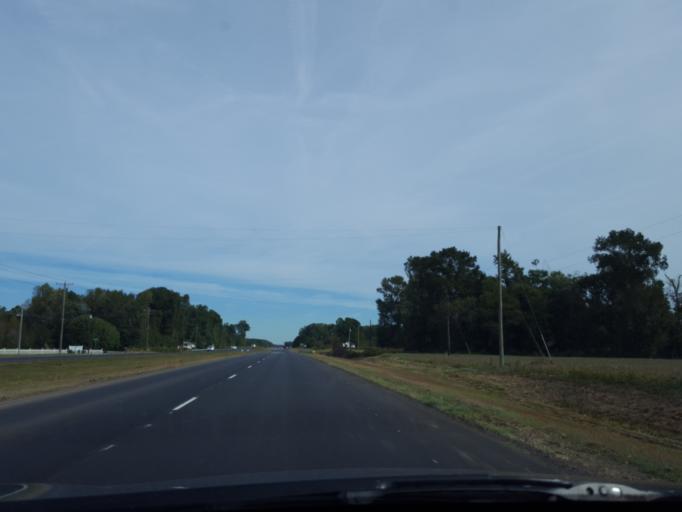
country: US
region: North Carolina
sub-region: Chowan County
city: Edenton
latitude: 36.1054
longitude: -76.5261
